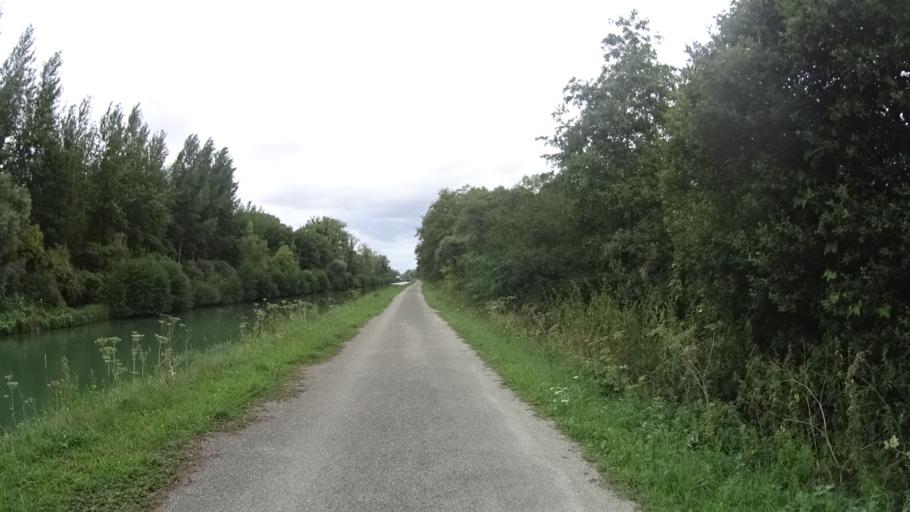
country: FR
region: Picardie
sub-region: Departement de l'Aisne
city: La Fere
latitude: 49.6710
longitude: 3.3558
